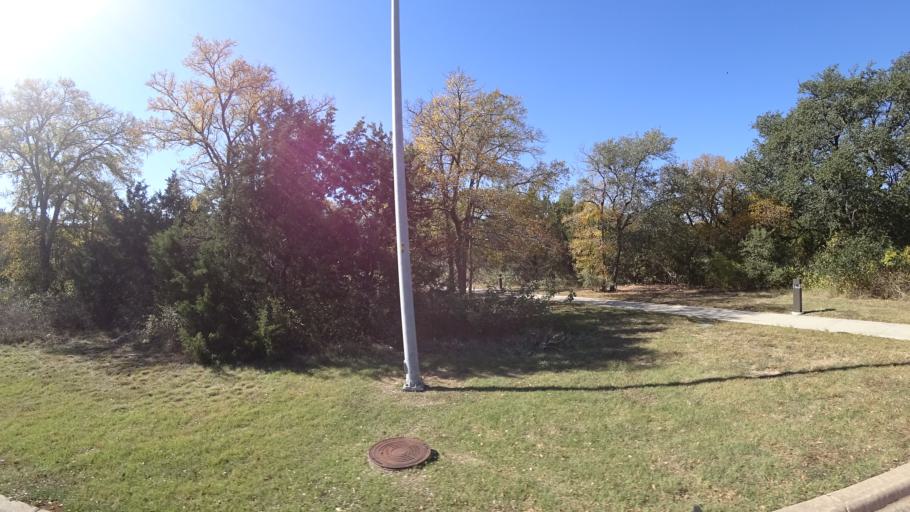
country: US
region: Texas
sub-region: Travis County
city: Wells Branch
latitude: 30.4454
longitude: -97.6918
